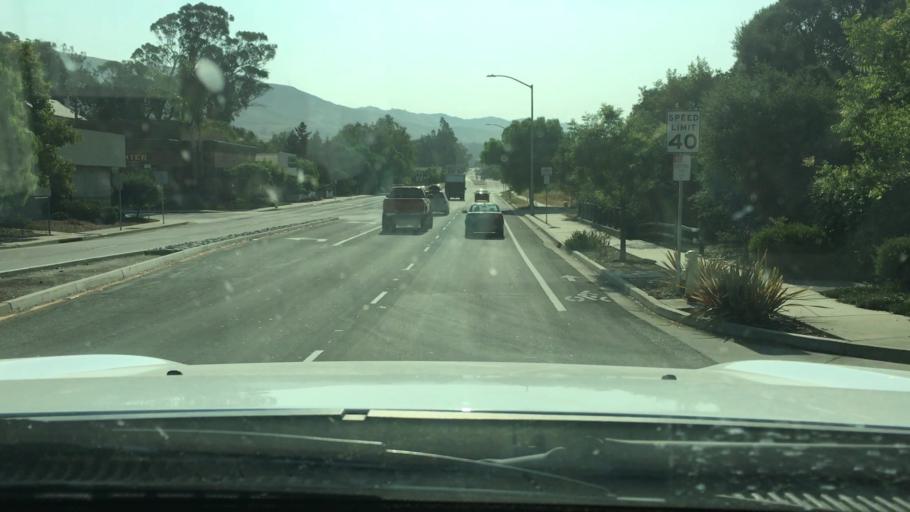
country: US
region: California
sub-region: San Luis Obispo County
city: San Luis Obispo
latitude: 35.2613
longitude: -120.6489
